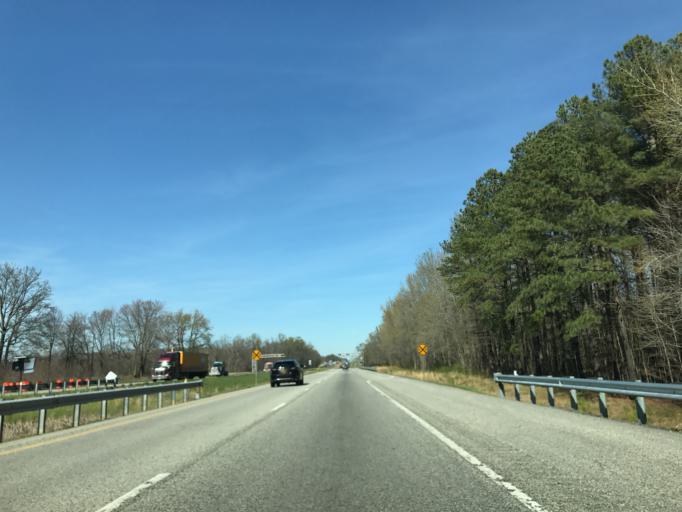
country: US
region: Maryland
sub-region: Queen Anne's County
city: Centreville
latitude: 39.0361
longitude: -76.0182
